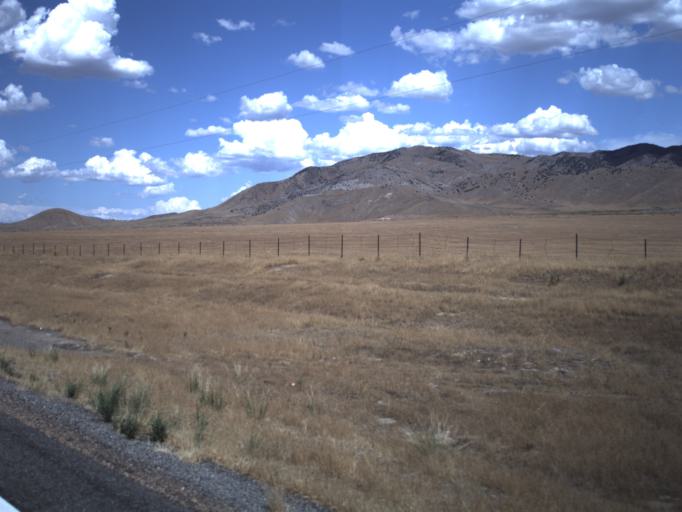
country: US
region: Utah
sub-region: Millard County
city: Delta
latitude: 39.6153
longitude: -112.3174
